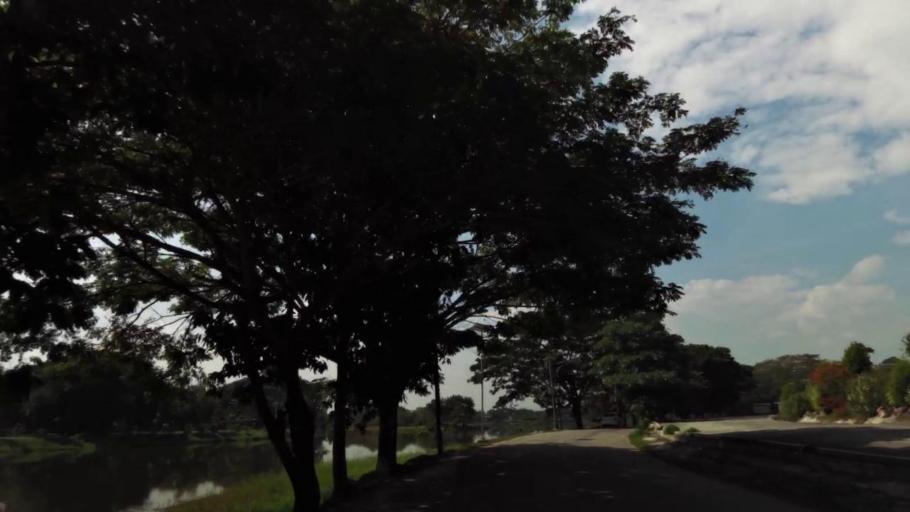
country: TH
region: Chiang Rai
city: Chiang Rai
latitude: 19.8862
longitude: 99.8070
